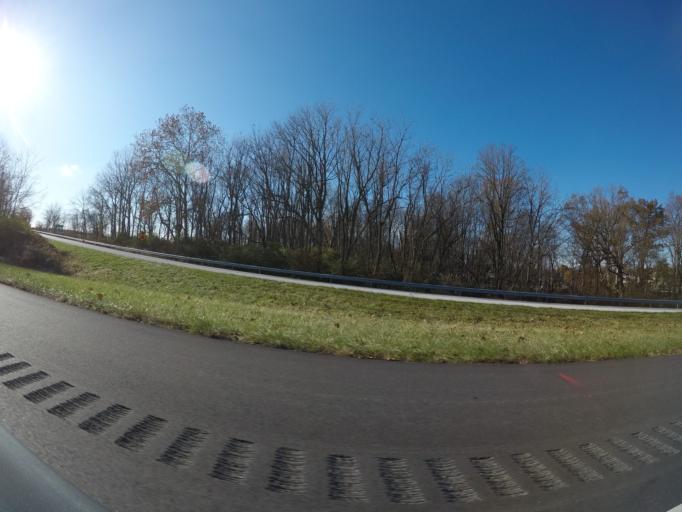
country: US
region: Pennsylvania
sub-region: Chester County
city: Oxford
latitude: 39.7539
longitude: -76.0235
